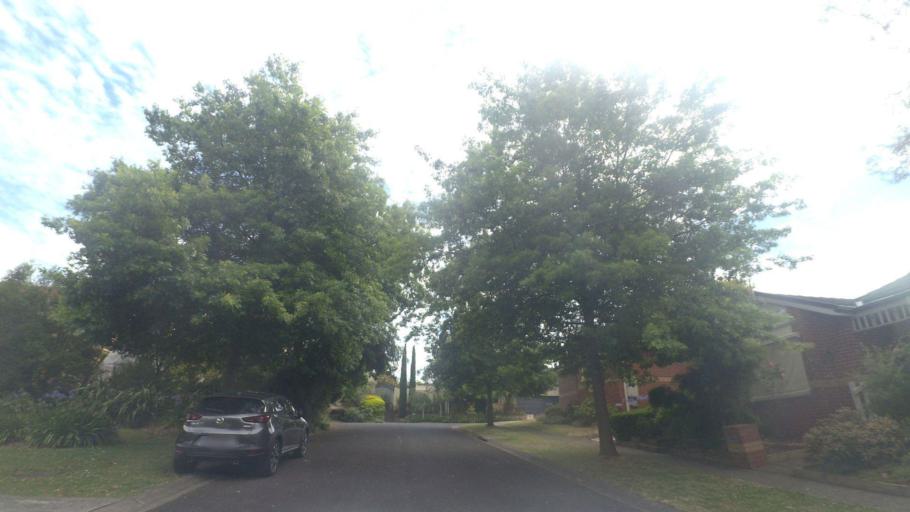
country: AU
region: Victoria
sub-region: Banyule
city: Viewbank
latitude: -37.7423
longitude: 145.0923
